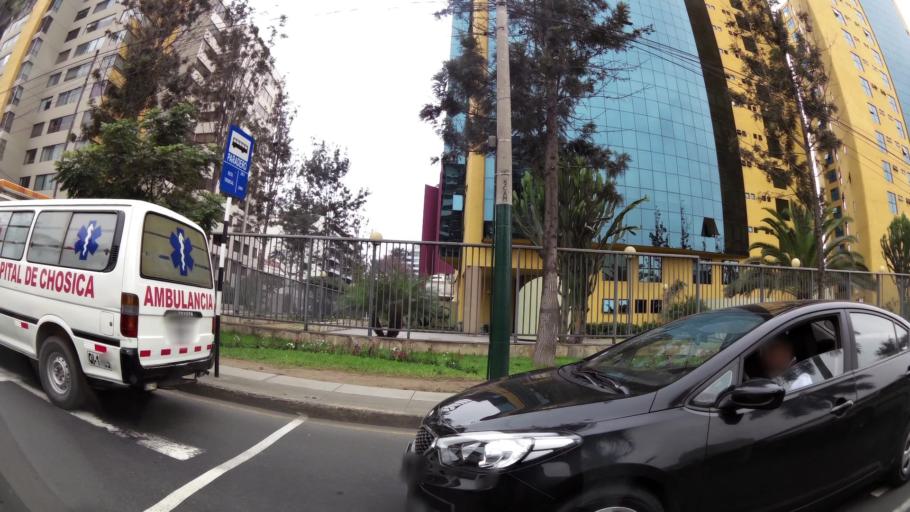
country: PE
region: Lima
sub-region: Lima
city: San Isidro
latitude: -12.0930
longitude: -77.0379
